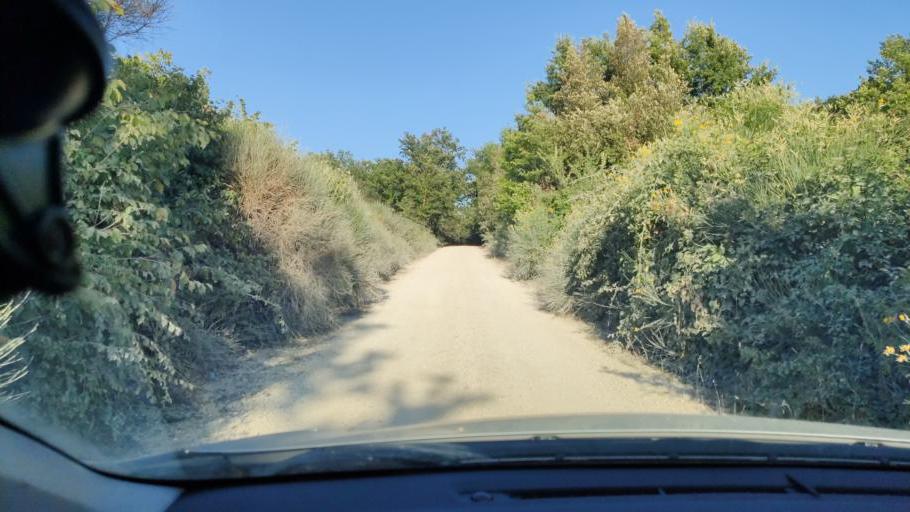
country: IT
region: Umbria
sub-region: Provincia di Terni
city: Penna in Teverina
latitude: 42.5398
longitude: 12.3684
